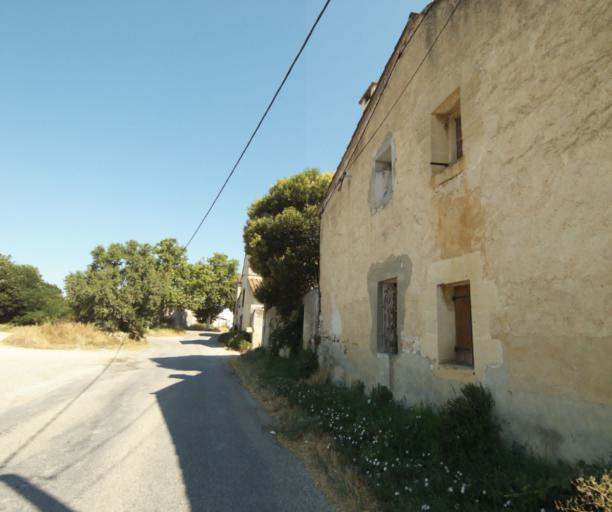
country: FR
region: Languedoc-Roussillon
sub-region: Departement de l'Herault
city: Marsillargues
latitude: 43.6620
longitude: 4.1628
